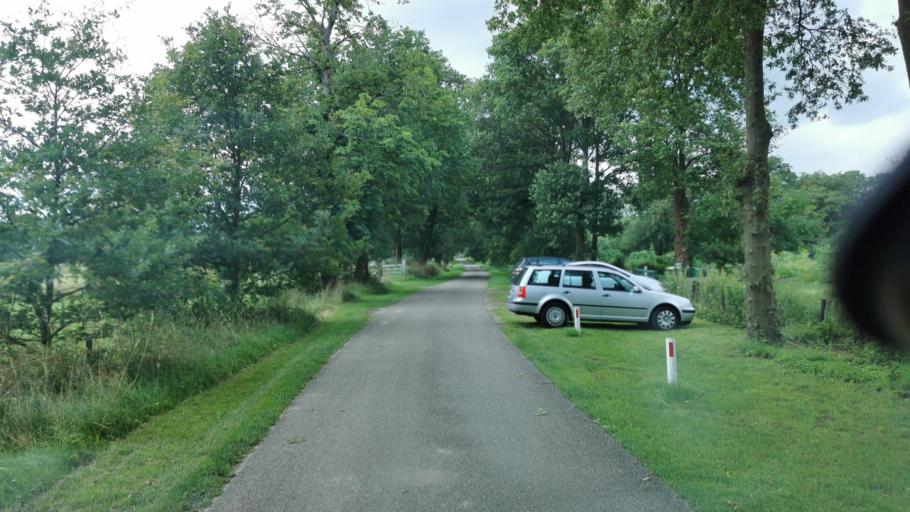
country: NL
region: Overijssel
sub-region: Gemeente Losser
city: Losser
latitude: 52.2457
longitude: 7.0043
